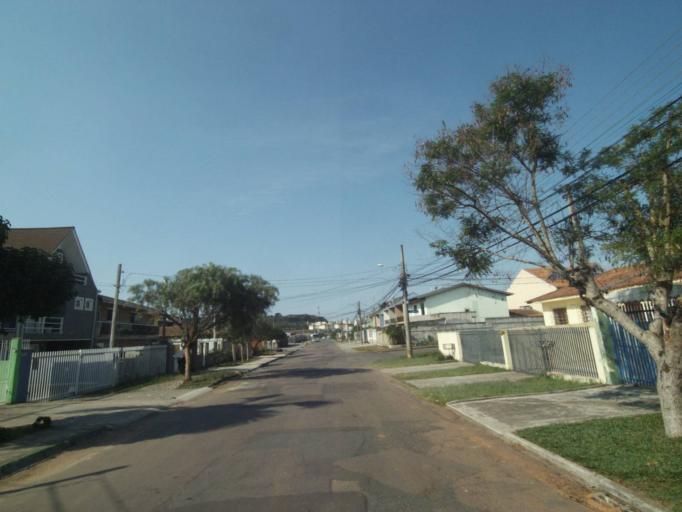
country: BR
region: Parana
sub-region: Curitiba
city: Curitiba
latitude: -25.4812
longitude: -49.3268
